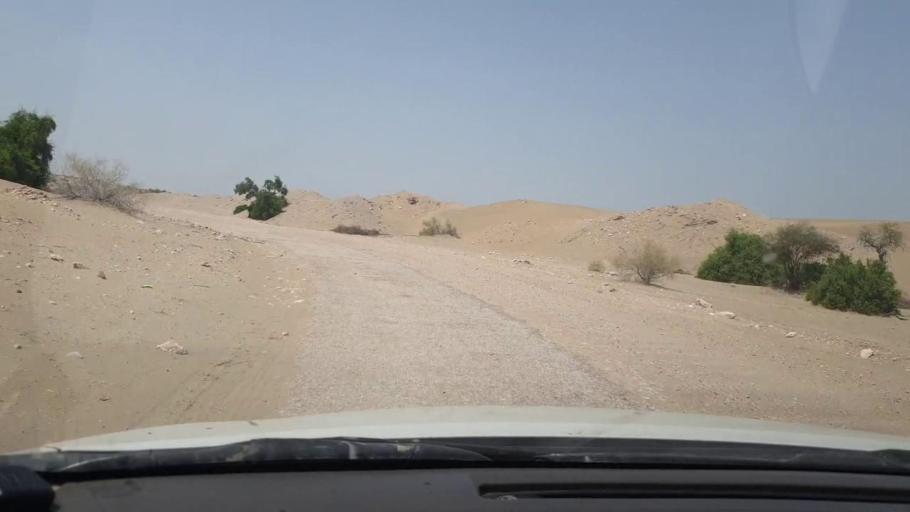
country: PK
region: Sindh
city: Rohri
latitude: 27.2871
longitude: 69.2375
